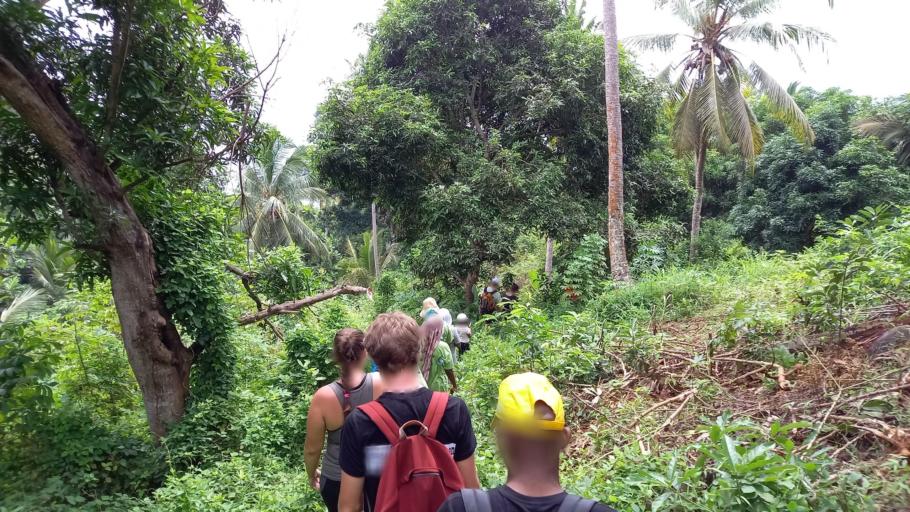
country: YT
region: Acoua
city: Acoua
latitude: -12.7112
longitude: 45.0565
